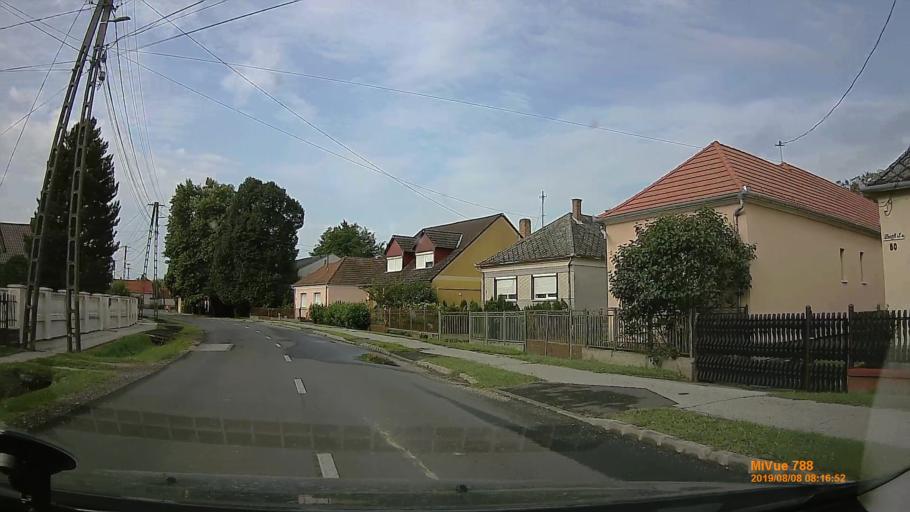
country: HR
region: Medimurska
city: Kotoriba
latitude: 46.3873
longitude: 16.8343
